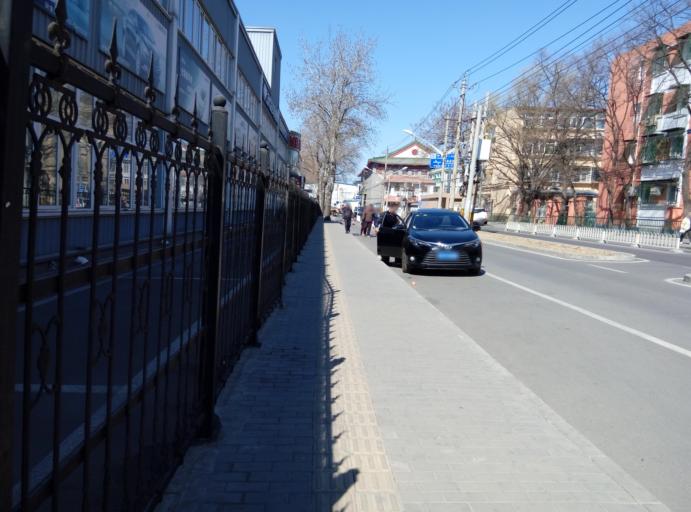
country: CN
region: Beijing
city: Haidian
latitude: 39.9913
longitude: 116.2864
